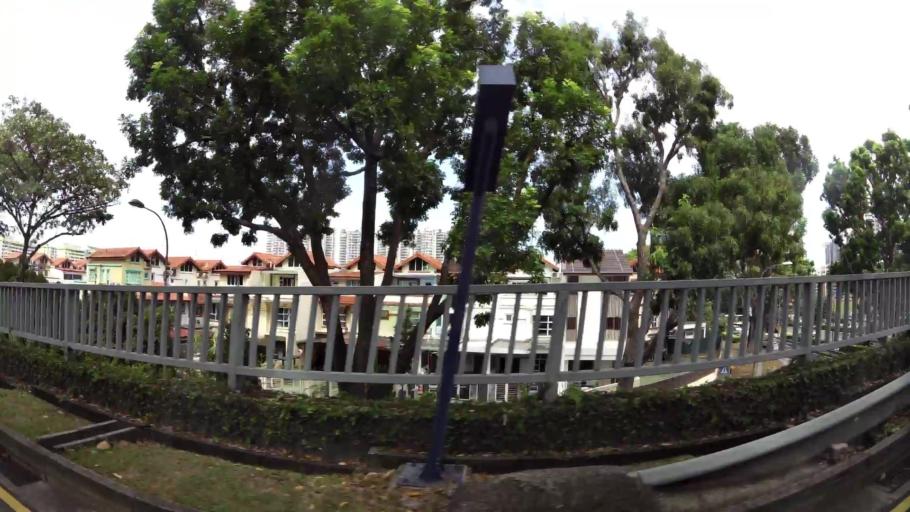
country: SG
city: Singapore
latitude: 1.3081
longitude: 103.7656
